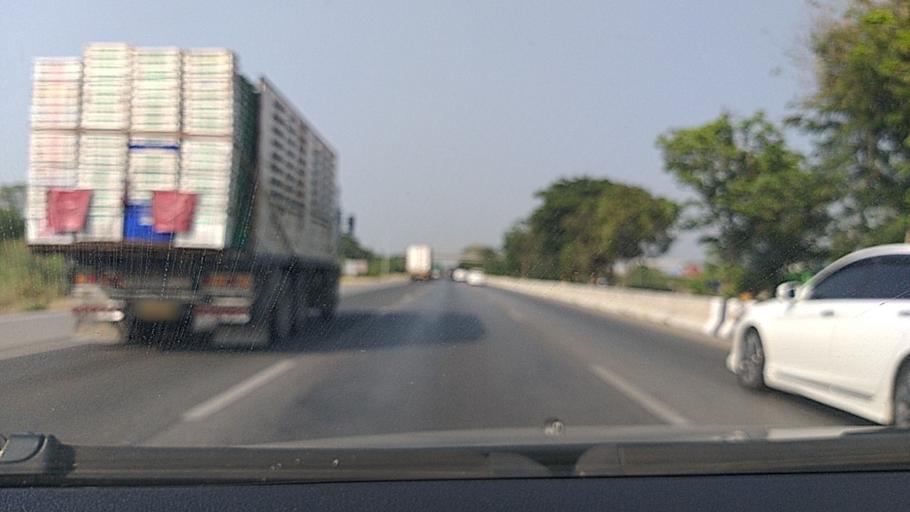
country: TH
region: Ang Thong
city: Ban Thai Tan
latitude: 14.6276
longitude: 100.4722
